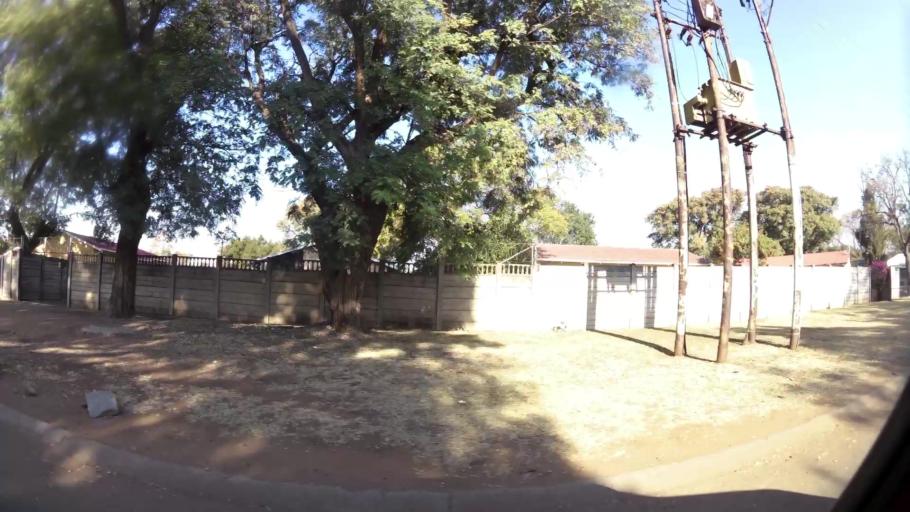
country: ZA
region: North-West
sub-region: Bojanala Platinum District Municipality
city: Rustenburg
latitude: -25.6474
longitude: 27.2308
